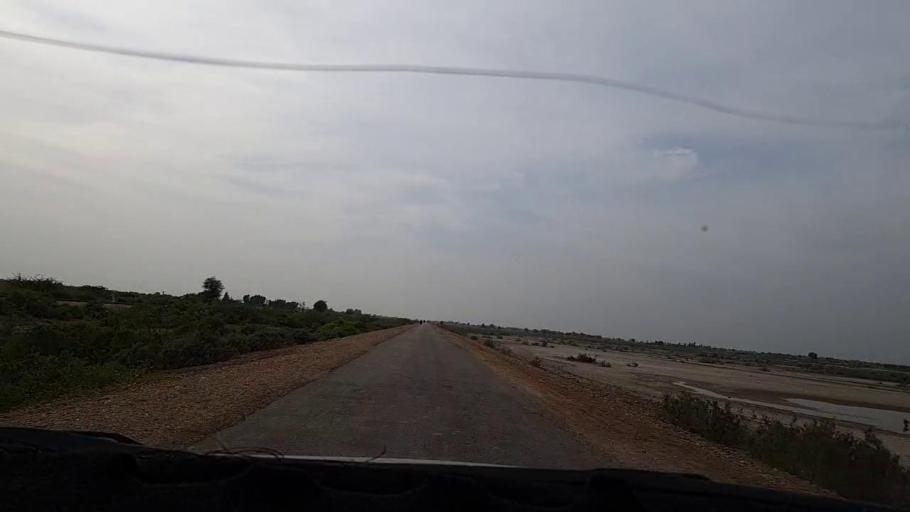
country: PK
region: Sindh
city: Pithoro
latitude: 25.5160
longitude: 69.2862
